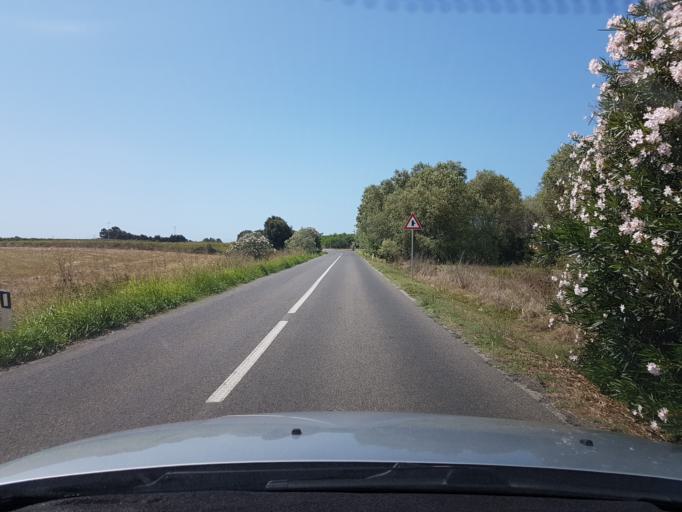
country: IT
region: Sardinia
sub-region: Provincia di Oristano
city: Riola Sardo
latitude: 40.0217
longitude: 8.4802
